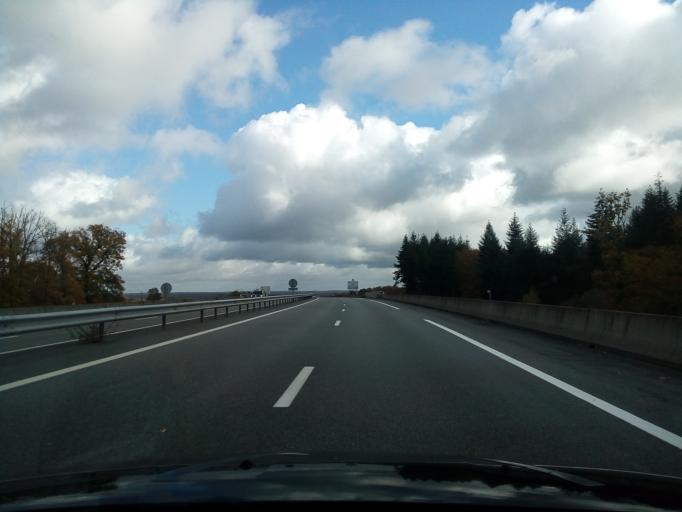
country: FR
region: Limousin
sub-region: Departement de la Creuse
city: Gouzon
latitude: 46.1941
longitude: 2.1765
